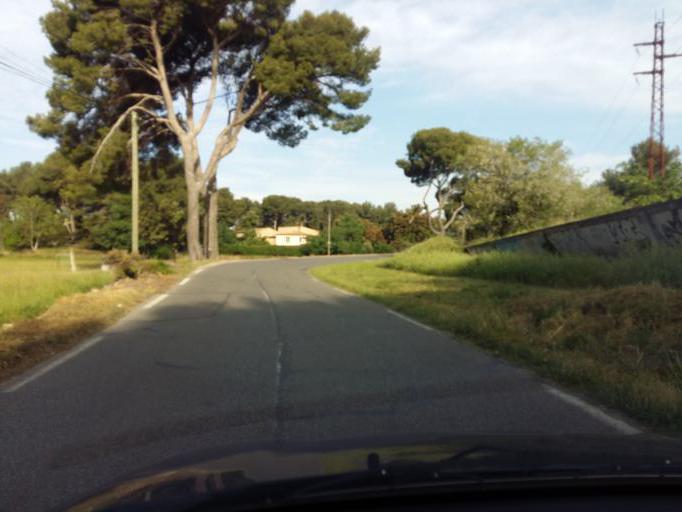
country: FR
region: Provence-Alpes-Cote d'Azur
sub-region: Departement des Bouches-du-Rhone
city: Pelissanne
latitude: 43.6361
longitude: 5.1245
